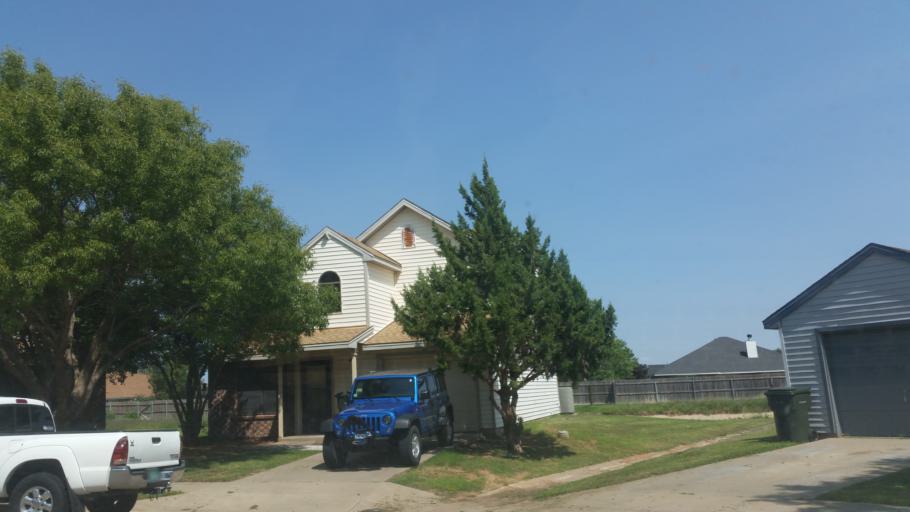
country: US
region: New Mexico
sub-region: Curry County
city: Clovis
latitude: 34.4451
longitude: -103.1734
